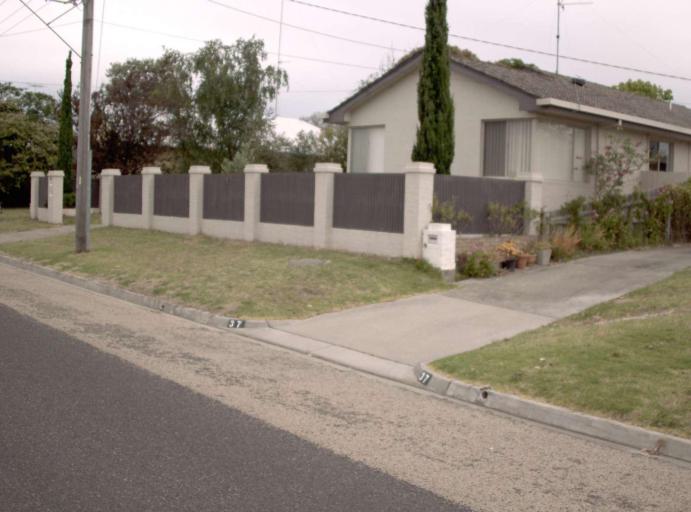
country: AU
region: Victoria
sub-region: East Gippsland
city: Bairnsdale
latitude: -37.9159
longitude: 147.7189
